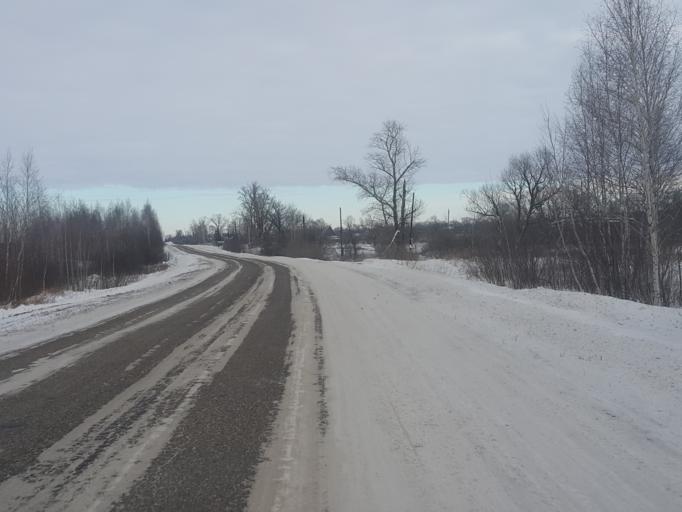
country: RU
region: Tambov
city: Platonovka
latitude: 52.8555
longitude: 41.8275
